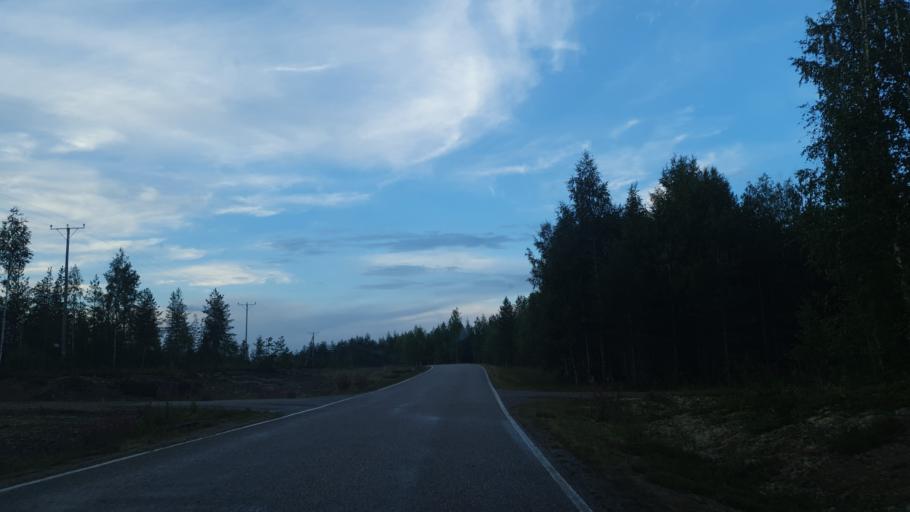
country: FI
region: Kainuu
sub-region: Kehys-Kainuu
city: Kuhmo
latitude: 63.8582
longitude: 29.8338
